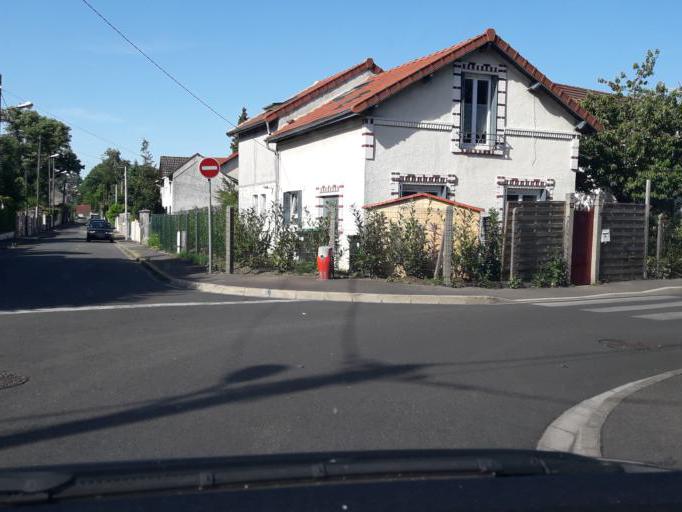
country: FR
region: Ile-de-France
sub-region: Departement de l'Essonne
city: Villemoisson-sur-Orge
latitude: 48.6547
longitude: 2.3347
